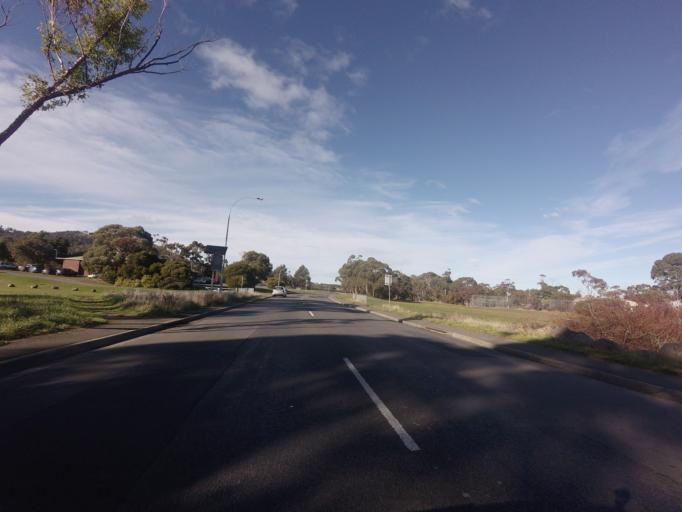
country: AU
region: Tasmania
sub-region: Clarence
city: Rokeby
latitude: -42.8947
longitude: 147.4449
